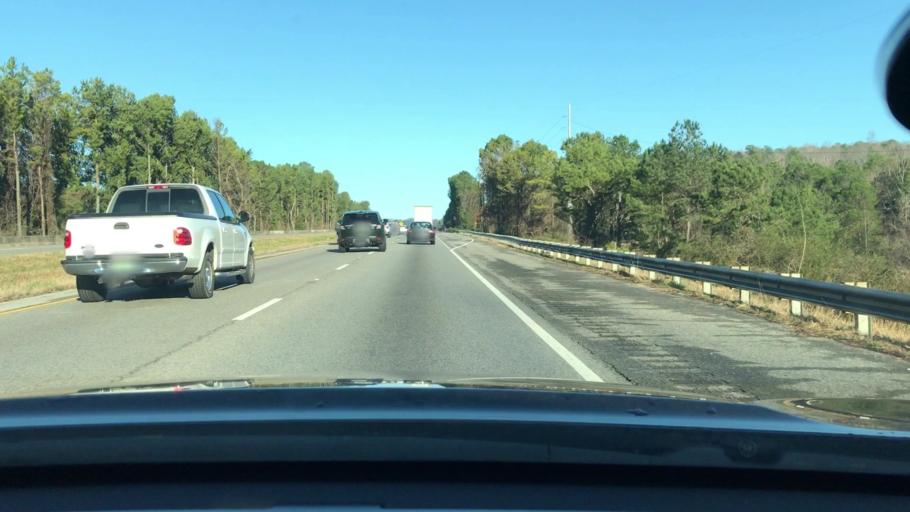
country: US
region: Alabama
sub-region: Shelby County
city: Chelsea
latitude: 33.3615
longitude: -86.6567
